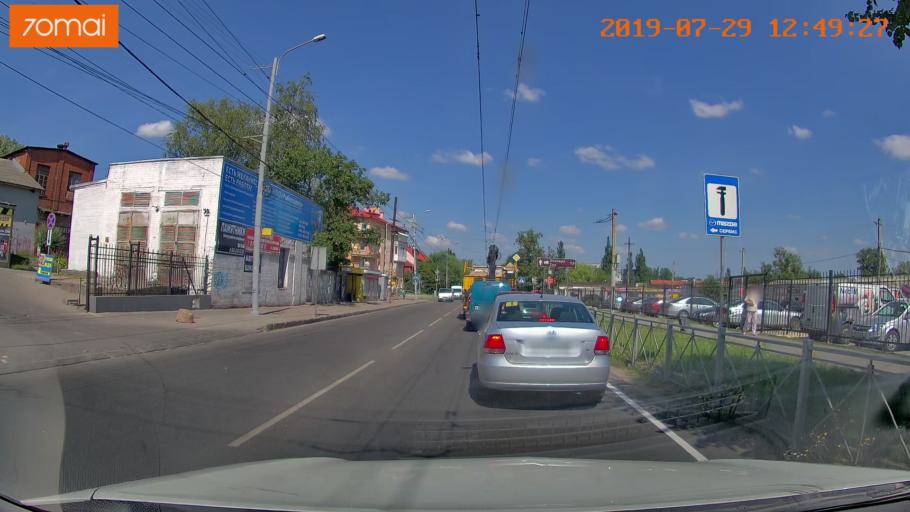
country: RU
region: Kaliningrad
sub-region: Gorod Kaliningrad
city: Kaliningrad
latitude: 54.6843
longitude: 20.5338
